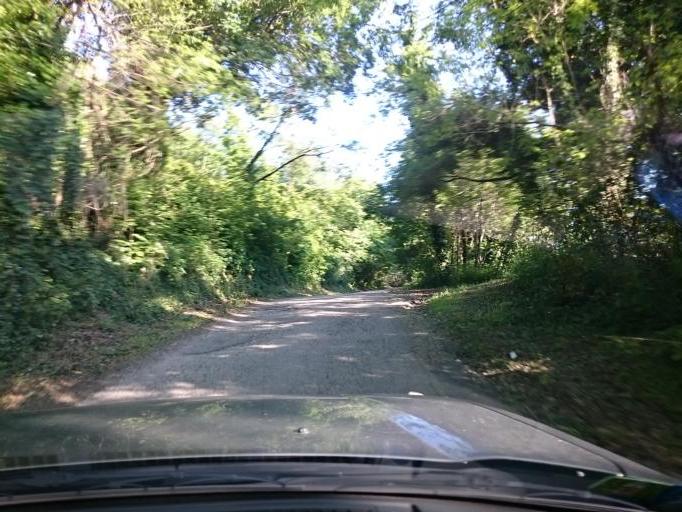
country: IT
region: Veneto
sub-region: Provincia di Padova
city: Galzignano
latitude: 45.3022
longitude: 11.7009
